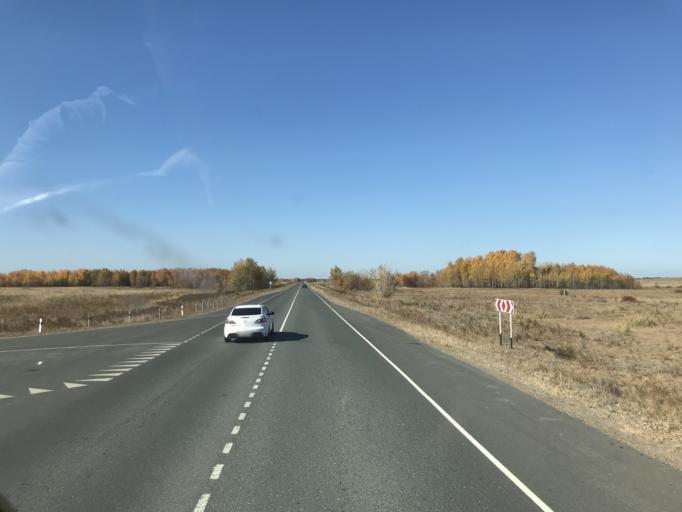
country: KZ
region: East Kazakhstan
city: Semey
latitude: 50.7076
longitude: 79.7327
